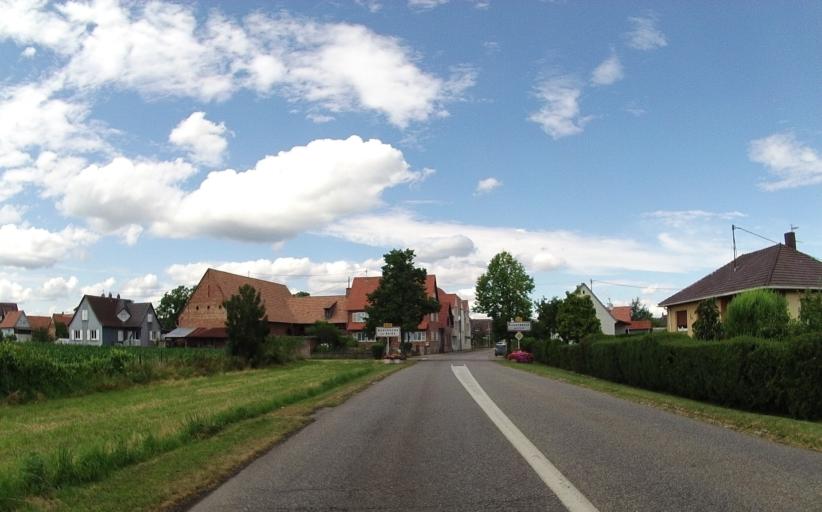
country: FR
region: Alsace
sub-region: Departement du Bas-Rhin
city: Durrenbach
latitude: 48.8989
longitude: 7.7455
